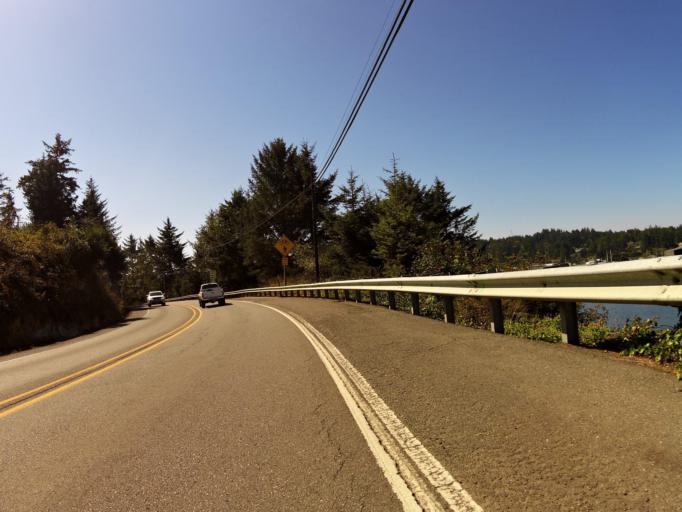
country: US
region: Oregon
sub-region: Coos County
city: Barview
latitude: 43.3410
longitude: -124.3169
